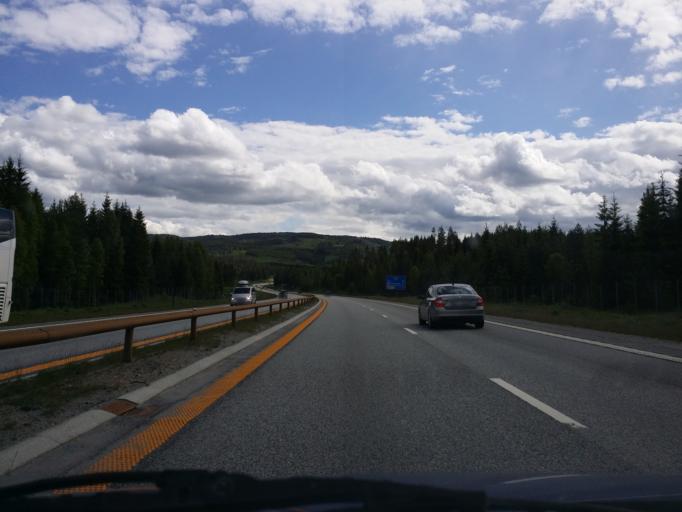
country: NO
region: Hedmark
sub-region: Stange
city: Stange
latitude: 60.6180
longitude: 11.3009
